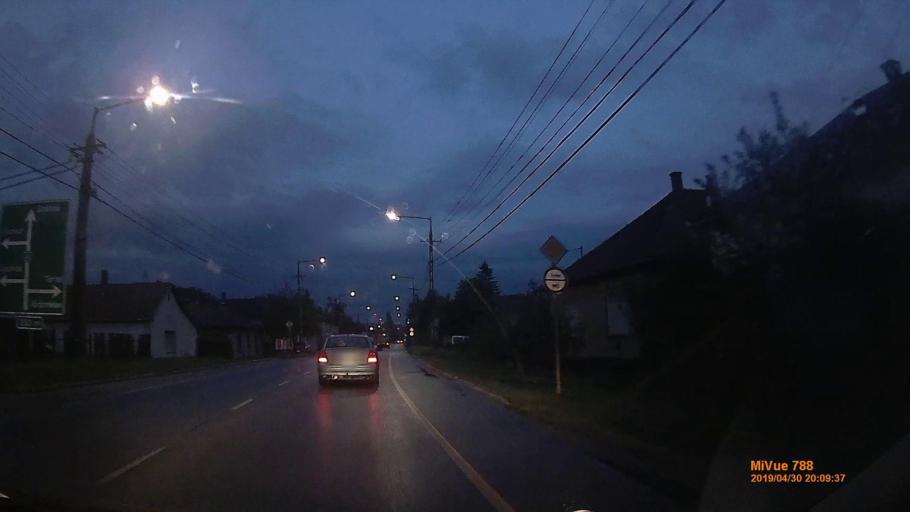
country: HU
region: Pest
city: Abony
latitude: 47.1835
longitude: 20.0637
